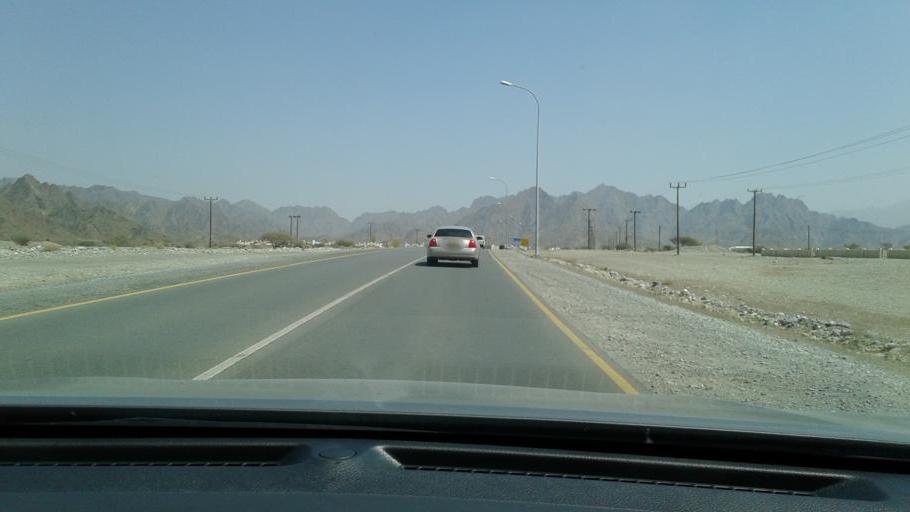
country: OM
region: Al Batinah
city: Rustaq
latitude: 23.3674
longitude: 57.4656
